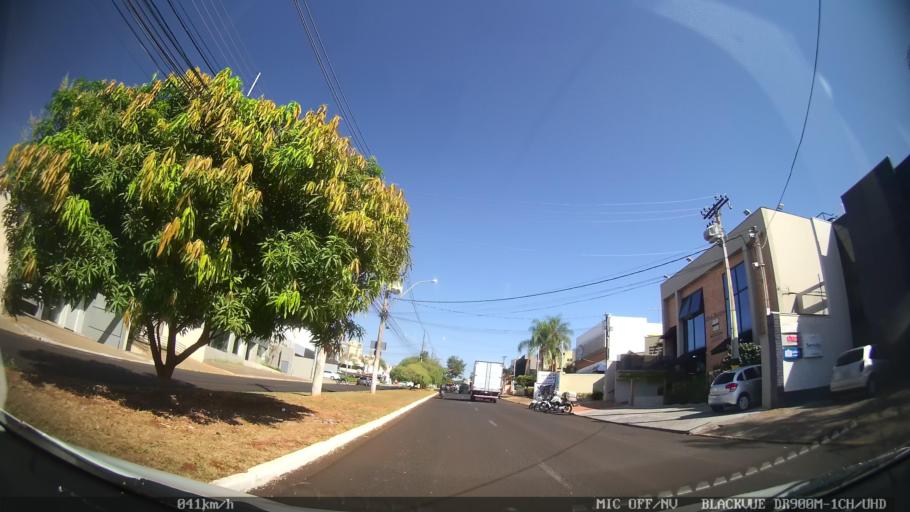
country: BR
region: Sao Paulo
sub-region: Ribeirao Preto
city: Ribeirao Preto
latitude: -21.2000
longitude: -47.8021
